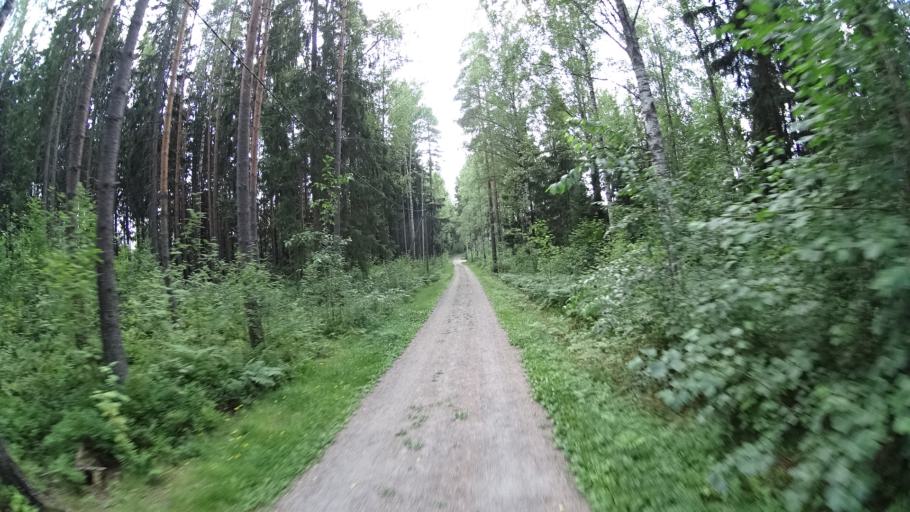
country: FI
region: Uusimaa
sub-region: Porvoo
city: Porvoo
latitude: 60.3811
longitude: 25.6982
